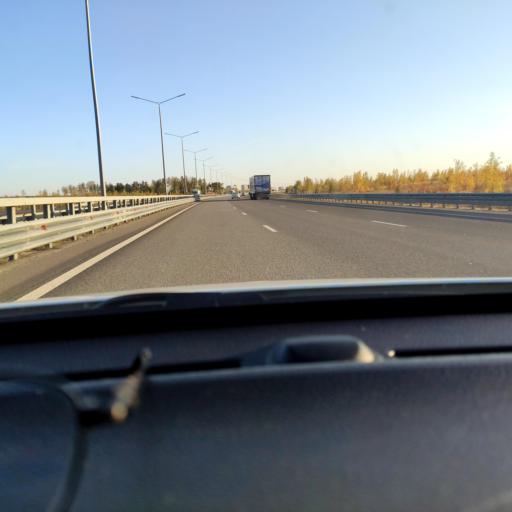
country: RU
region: Voronezj
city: Somovo
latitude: 51.7647
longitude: 39.3056
